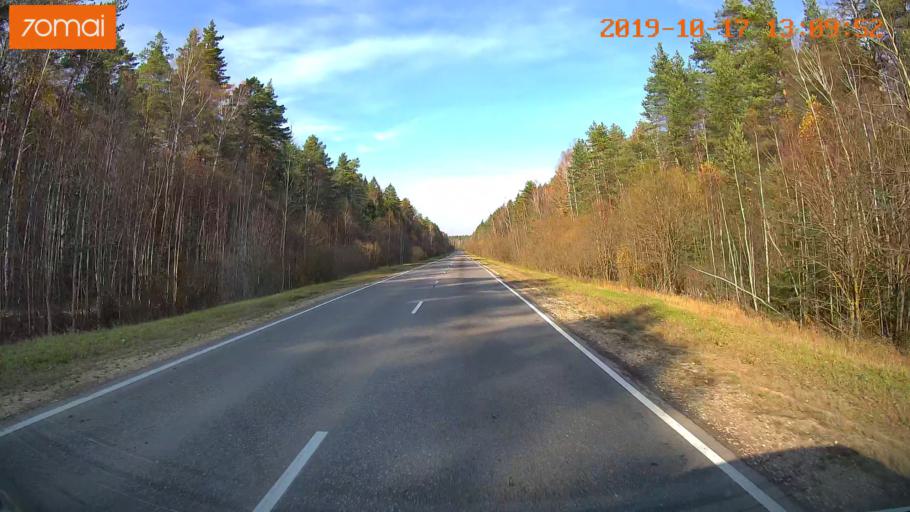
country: RU
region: Rjazan
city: Syntul
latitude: 55.0104
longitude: 41.2602
